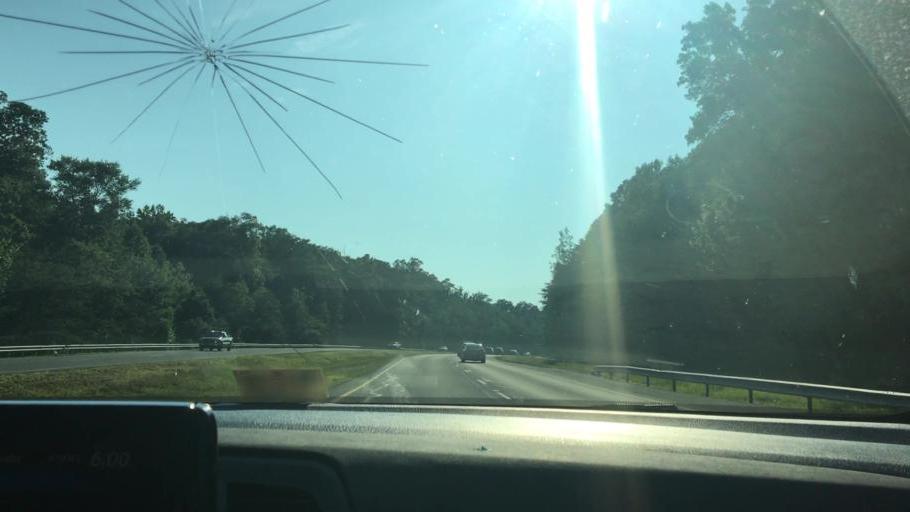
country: US
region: Virginia
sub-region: Prince William County
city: Buckhall
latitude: 38.6870
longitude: -77.3808
